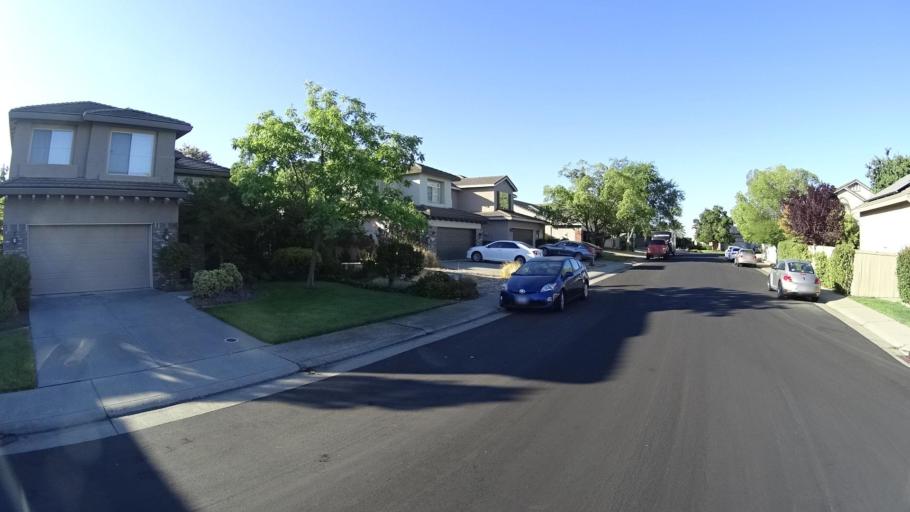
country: US
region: California
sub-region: Placer County
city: Rocklin
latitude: 38.8209
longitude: -121.2690
